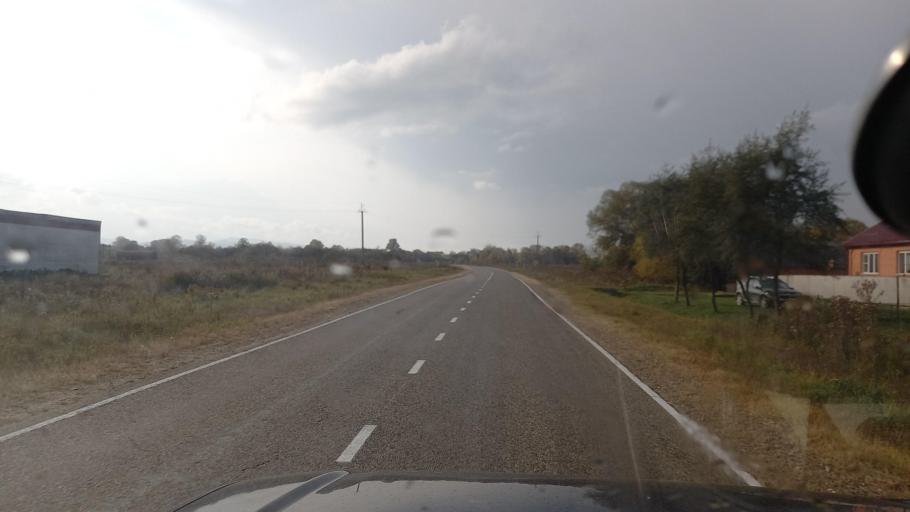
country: RU
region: Krasnodarskiy
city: Gubskaya
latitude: 44.3190
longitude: 40.5998
